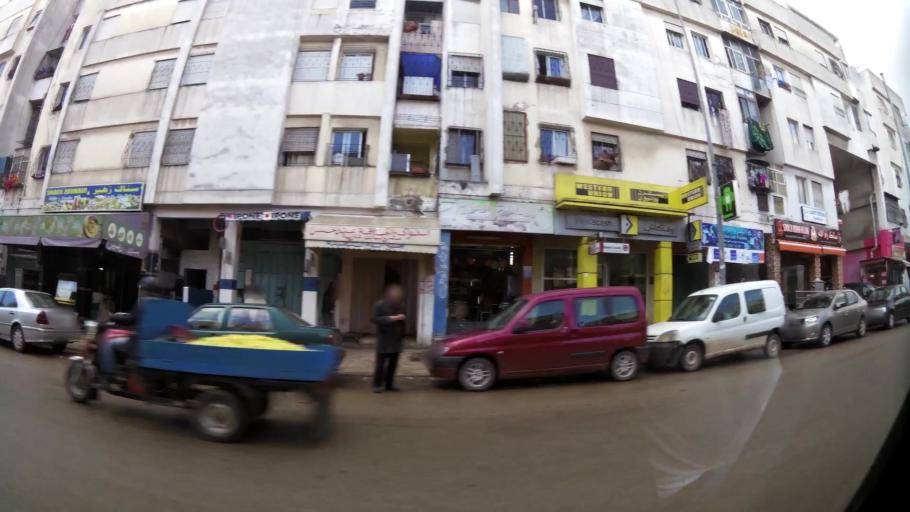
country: MA
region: Grand Casablanca
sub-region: Mediouna
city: Tit Mellil
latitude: 33.5862
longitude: -7.5266
